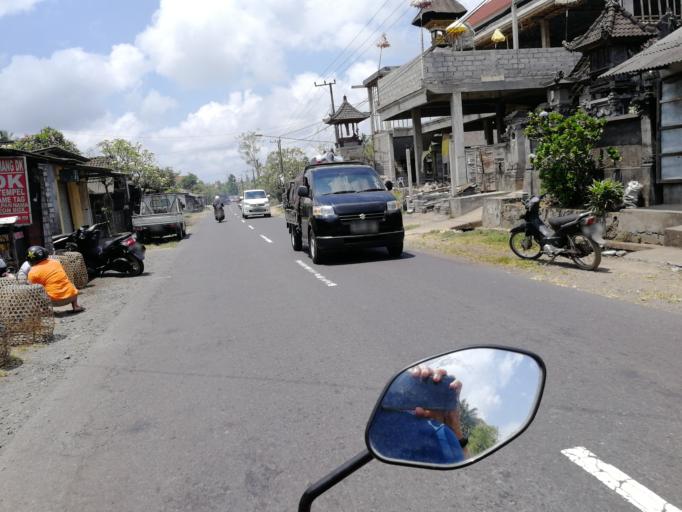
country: ID
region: Bali
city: Banjar Kubu
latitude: -8.4365
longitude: 115.4159
